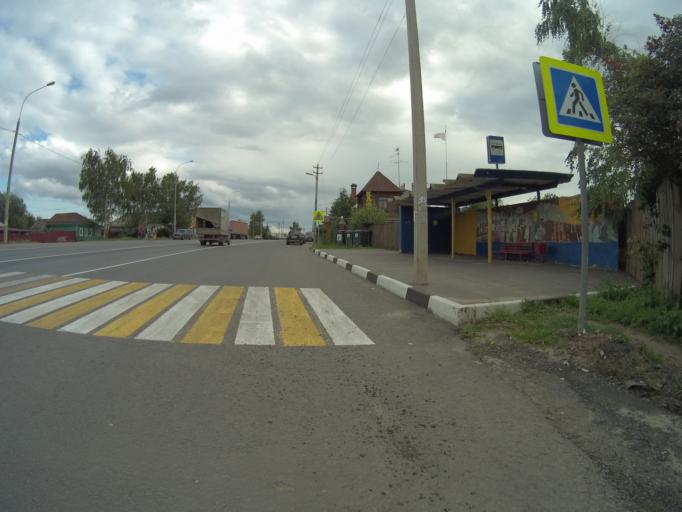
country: RU
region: Vladimir
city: Suzdal'
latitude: 56.3179
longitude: 40.4735
